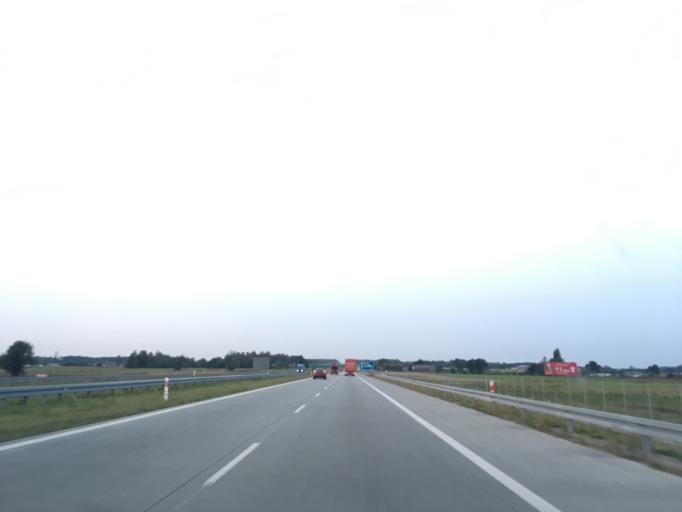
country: PL
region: Lodz Voivodeship
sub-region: Powiat lodzki wschodni
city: Brojce
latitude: 51.6876
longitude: 19.5960
